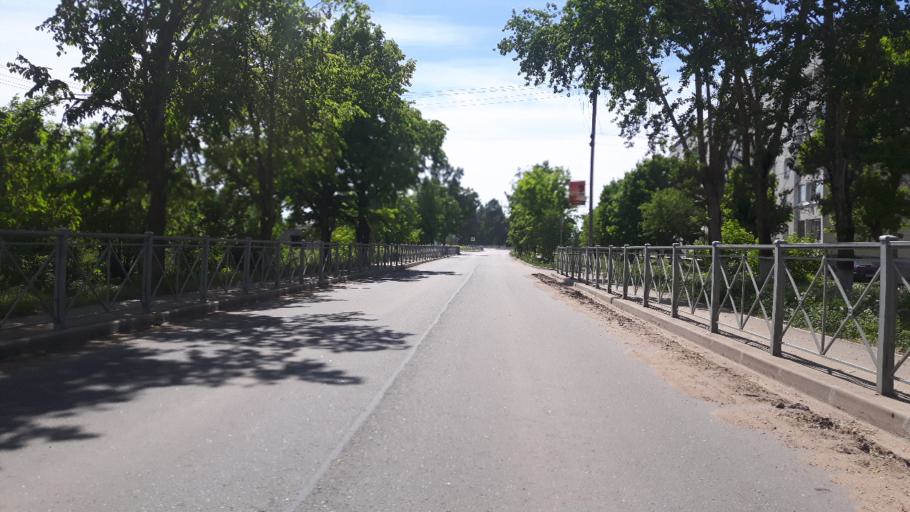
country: RU
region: Leningrad
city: Ust'-Luga
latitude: 59.5807
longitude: 28.1792
